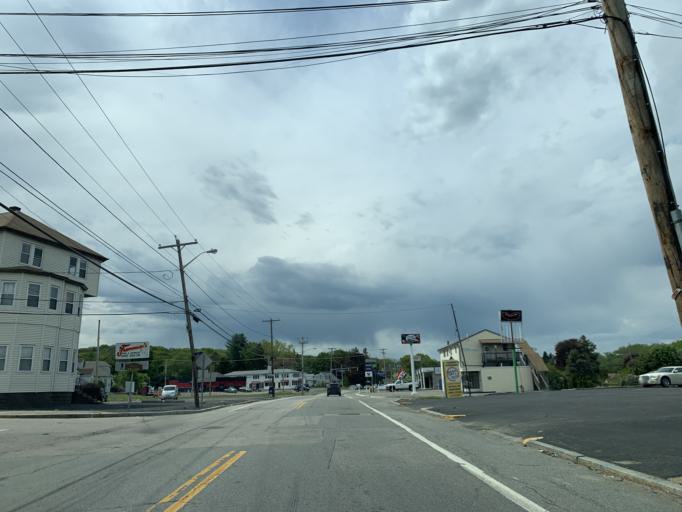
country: US
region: Rhode Island
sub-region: Providence County
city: Johnston
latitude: 41.8057
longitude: -71.4908
